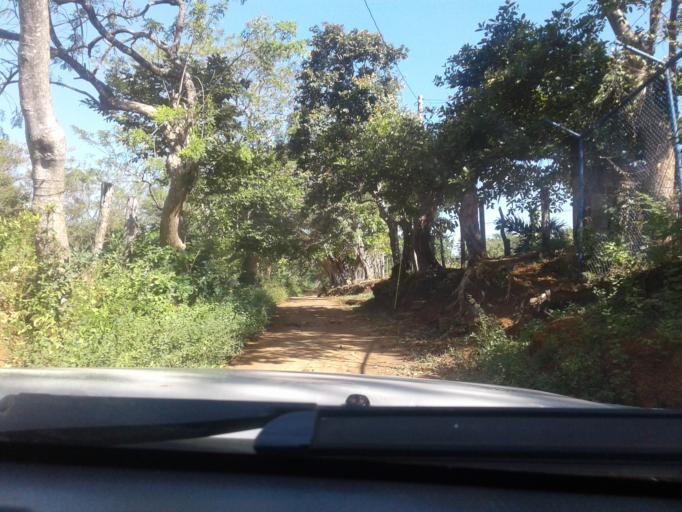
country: NI
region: Carazo
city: Santa Teresa
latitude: 11.7549
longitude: -86.1798
